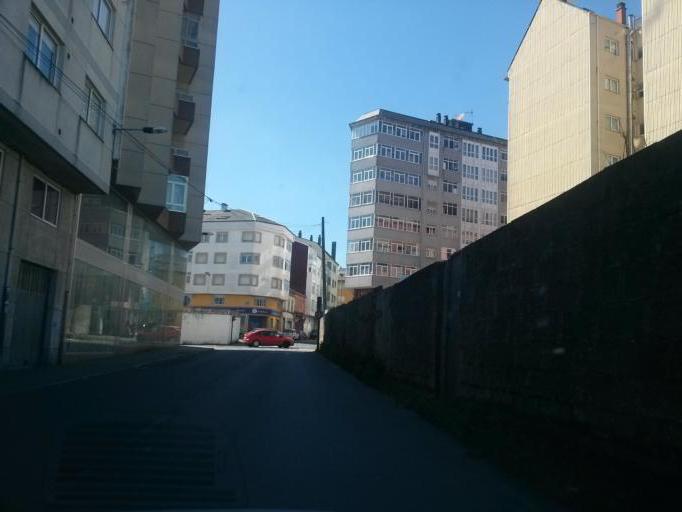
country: ES
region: Galicia
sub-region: Provincia de Lugo
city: Lugo
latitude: 43.0288
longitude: -7.5691
